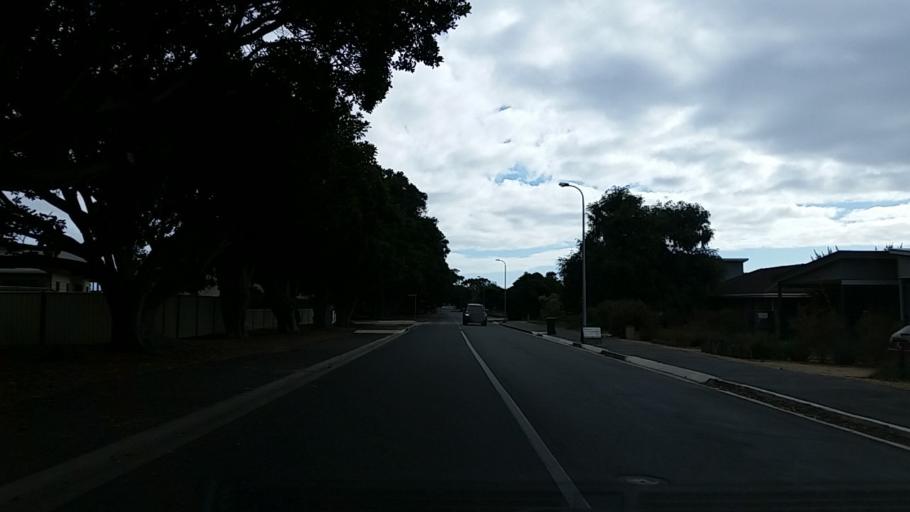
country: AU
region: South Australia
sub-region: Yankalilla
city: Normanville
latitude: -35.4448
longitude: 138.3158
